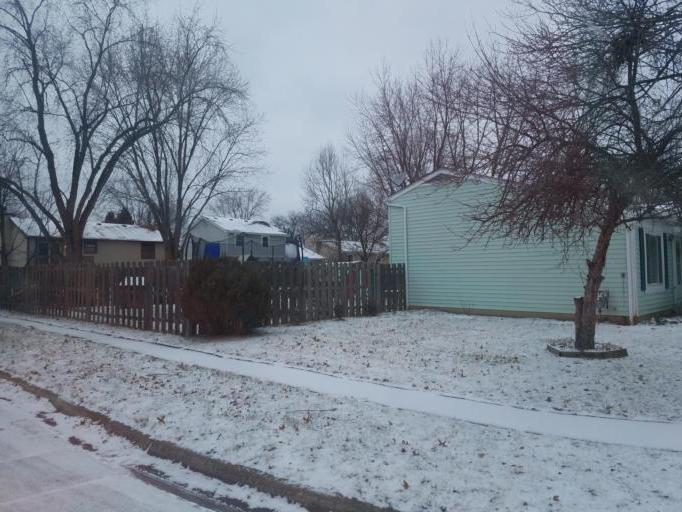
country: US
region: Ohio
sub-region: Delaware County
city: Powell
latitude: 40.1372
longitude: -83.0657
